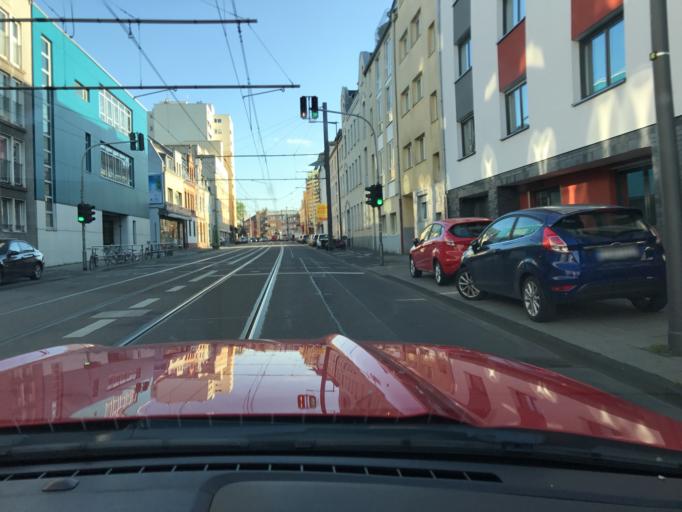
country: DE
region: North Rhine-Westphalia
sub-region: Regierungsbezirk Koln
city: Nippes
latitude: 50.9822
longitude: 6.9477
